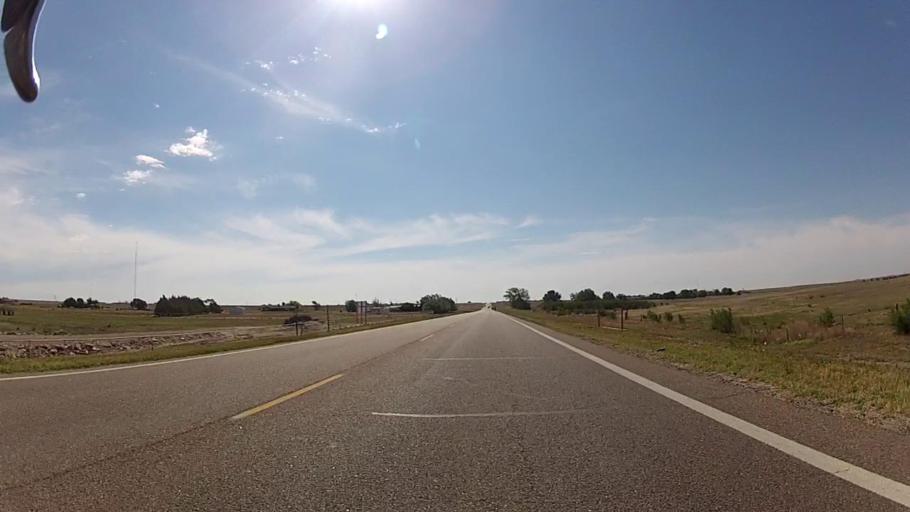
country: US
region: Kansas
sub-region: Grant County
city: Ulysses
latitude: 37.5708
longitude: -101.3314
